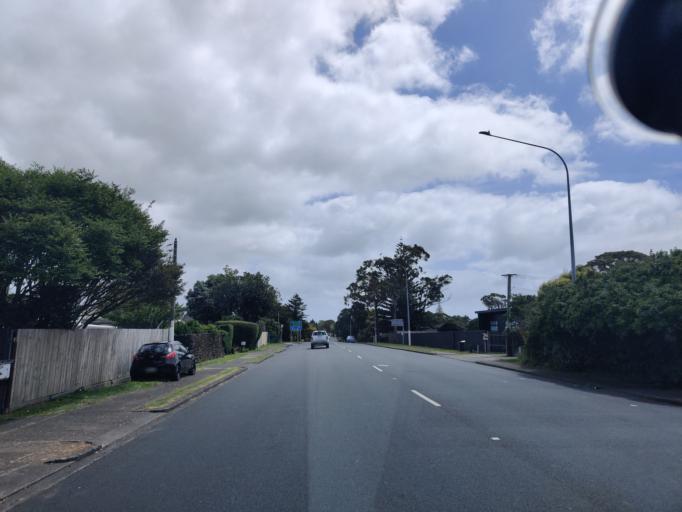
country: NZ
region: Auckland
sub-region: Auckland
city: Mangere
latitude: -36.9540
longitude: 174.7946
